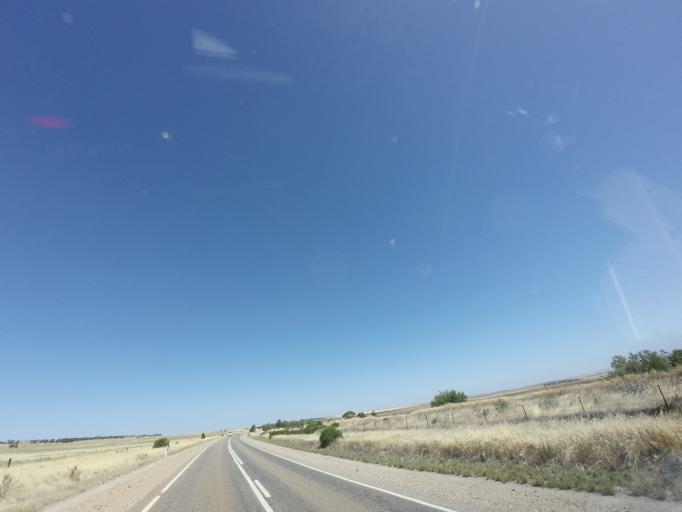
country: AU
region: South Australia
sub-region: Peterborough
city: Peterborough
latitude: -32.9491
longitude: 138.7887
